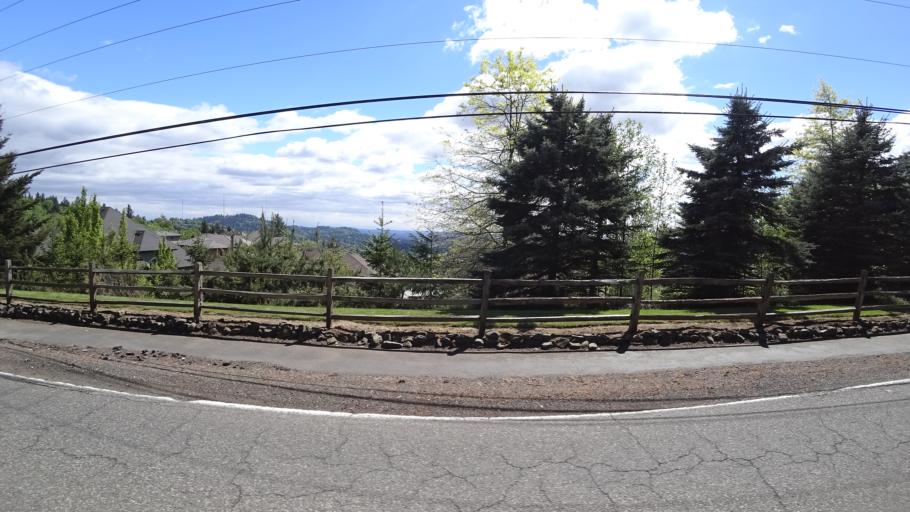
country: US
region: Oregon
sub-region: Washington County
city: West Haven
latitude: 45.5522
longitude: -122.7738
